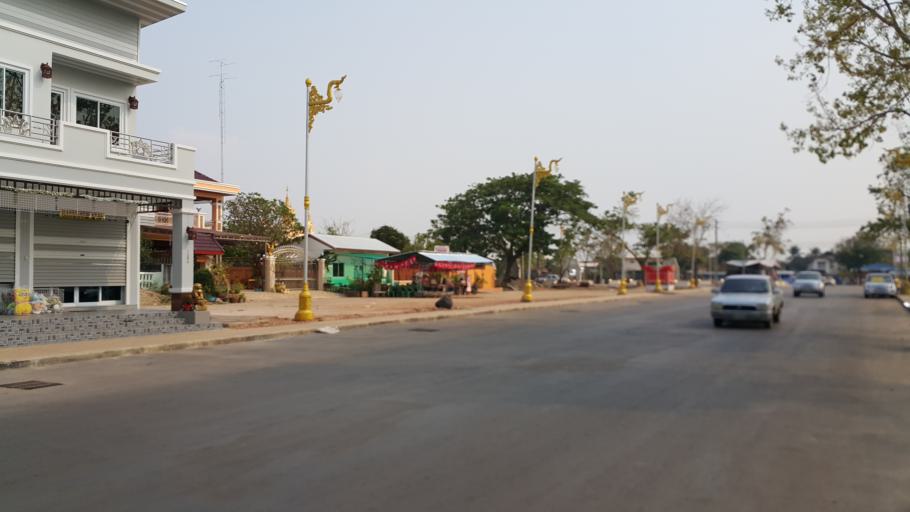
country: TH
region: Nakhon Phanom
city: That Phanom
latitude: 16.9437
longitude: 104.7272
